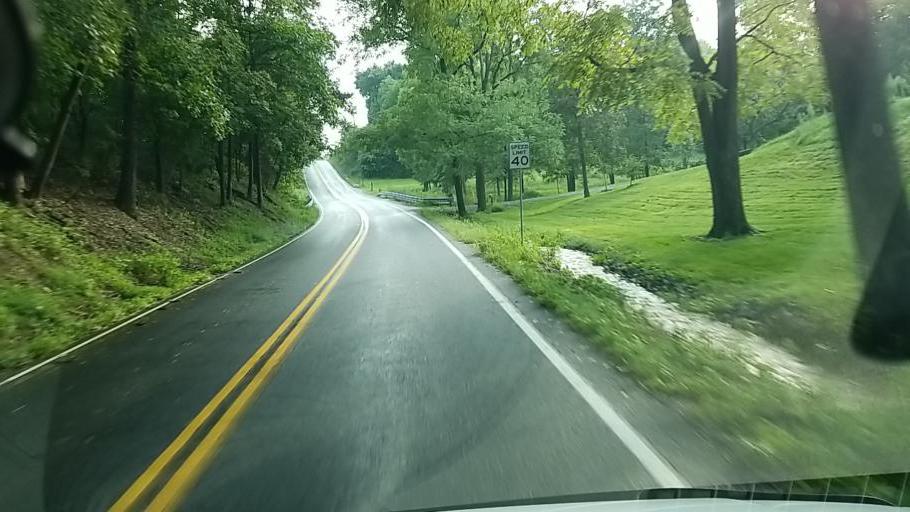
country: US
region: Pennsylvania
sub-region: Cumberland County
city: Newville
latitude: 40.1940
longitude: -77.4872
